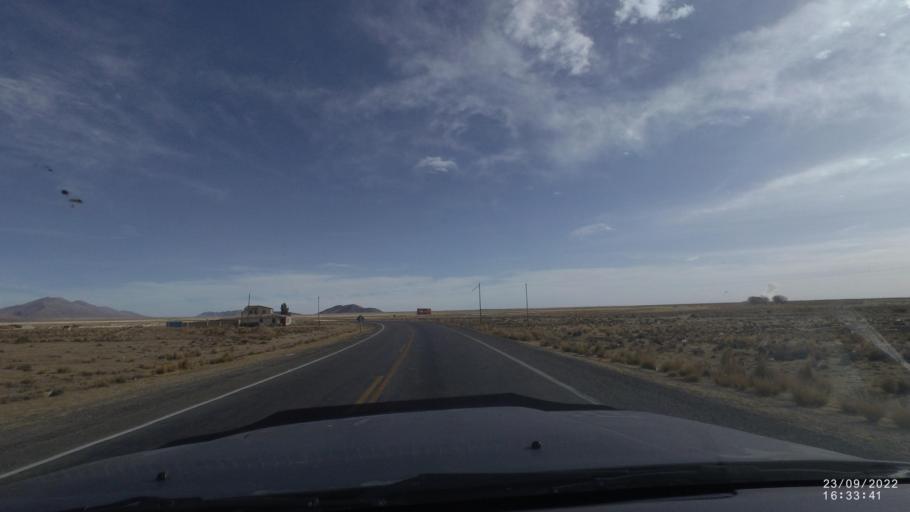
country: BO
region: Oruro
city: Machacamarca
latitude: -18.1777
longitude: -67.0155
